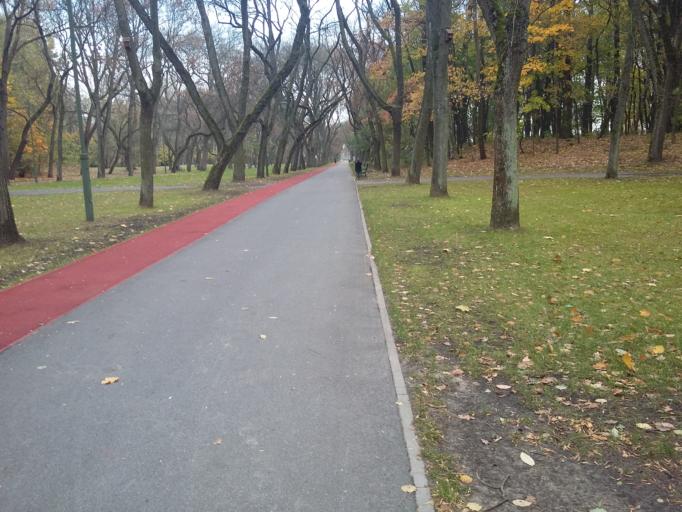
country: PL
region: Lodz Voivodeship
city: Lodz
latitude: 51.7629
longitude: 19.4184
